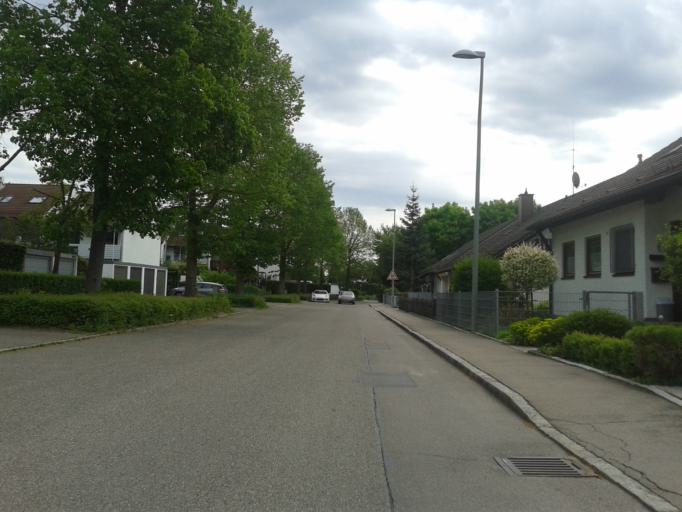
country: DE
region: Baden-Wuerttemberg
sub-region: Tuebingen Region
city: Erbach
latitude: 48.3552
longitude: 9.9085
